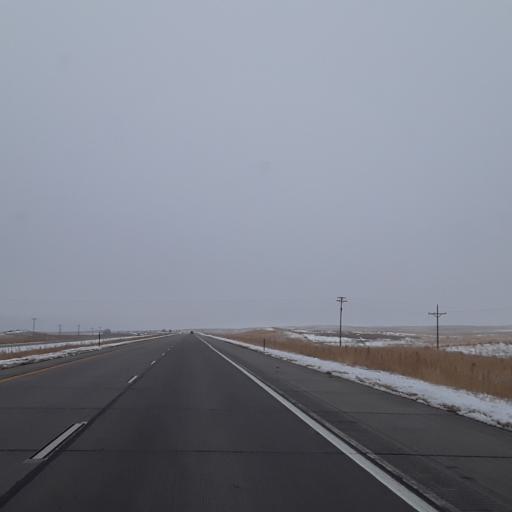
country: US
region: Colorado
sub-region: Logan County
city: Sterling
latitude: 40.5302
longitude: -103.2327
